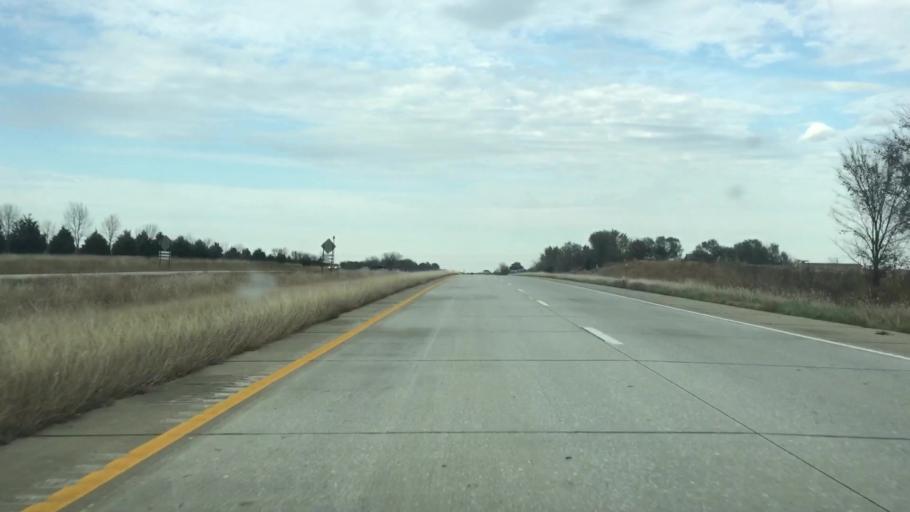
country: US
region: Missouri
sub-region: Henry County
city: Clinton
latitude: 38.2973
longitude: -93.7587
